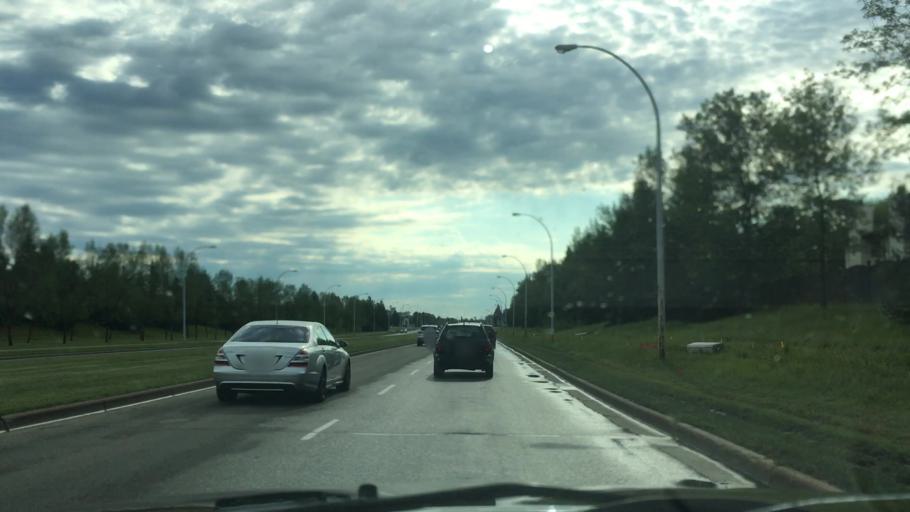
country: CA
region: Alberta
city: Edmonton
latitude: 53.4538
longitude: -113.5231
